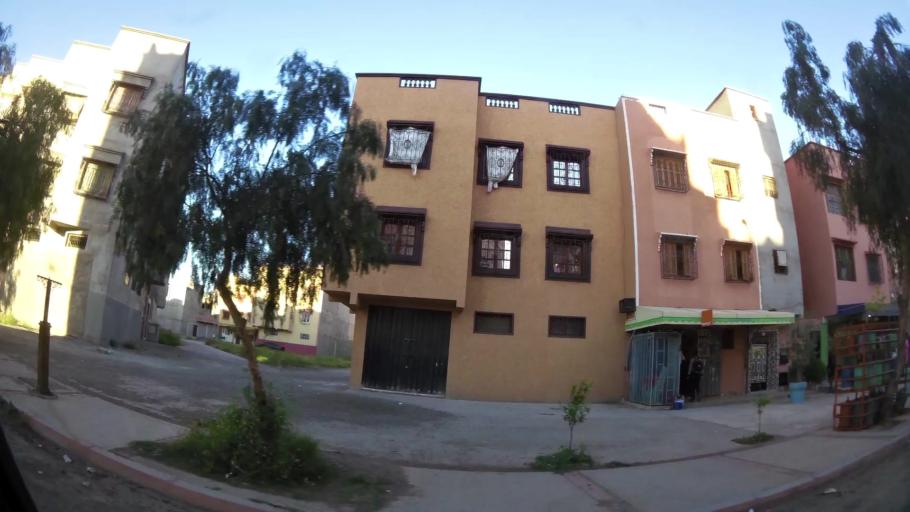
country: MA
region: Marrakech-Tensift-Al Haouz
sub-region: Marrakech
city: Marrakesh
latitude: 31.7439
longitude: -8.1099
